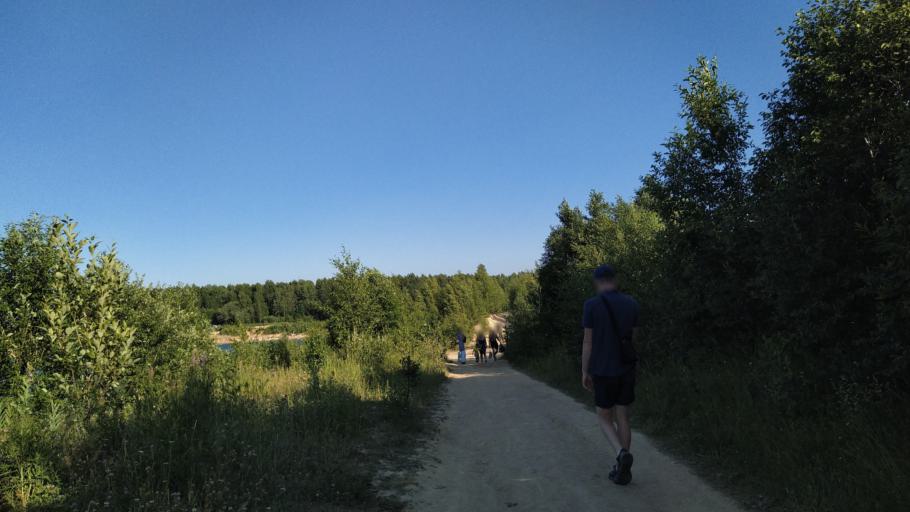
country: RU
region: Leningrad
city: Toksovo
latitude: 60.1153
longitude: 30.5366
